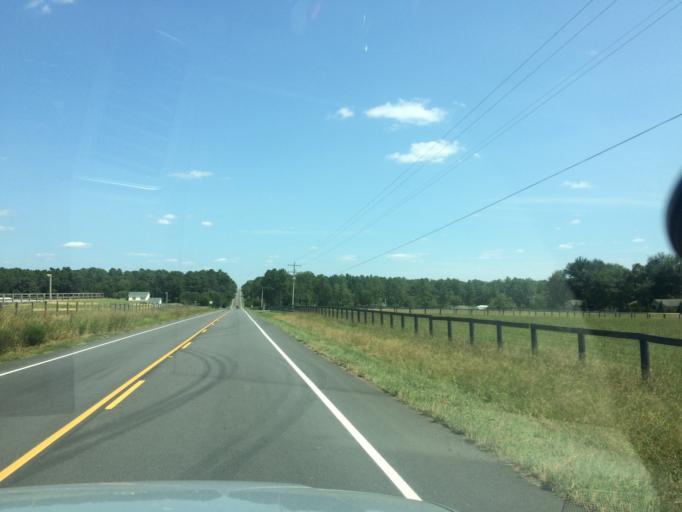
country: US
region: South Carolina
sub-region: Aiken County
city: Aiken
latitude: 33.5727
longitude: -81.5634
